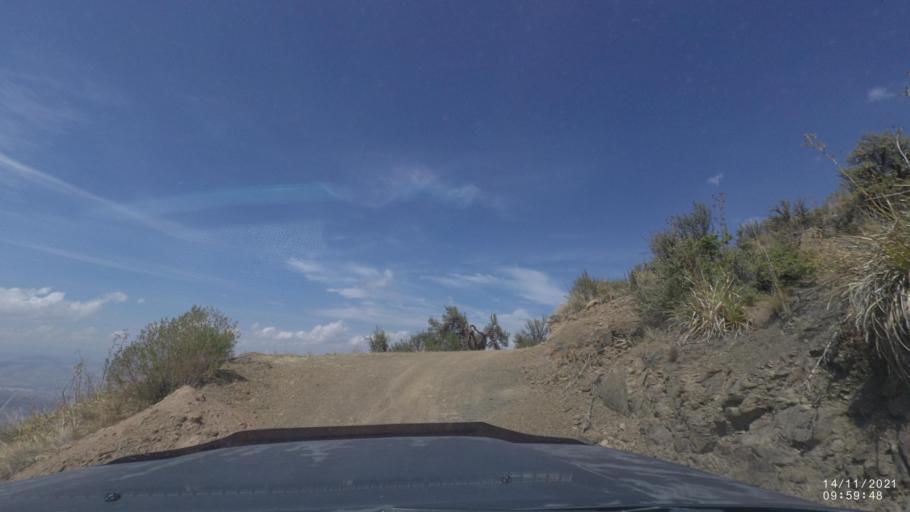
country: BO
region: Cochabamba
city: Cochabamba
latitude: -17.3540
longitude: -66.0891
